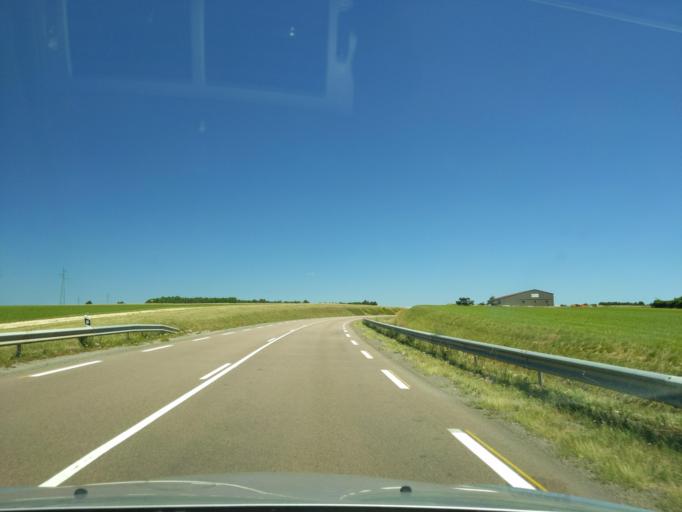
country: FR
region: Bourgogne
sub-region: Departement de la Cote-d'Or
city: Ruffey-les-Echirey
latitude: 47.4115
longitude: 5.0728
